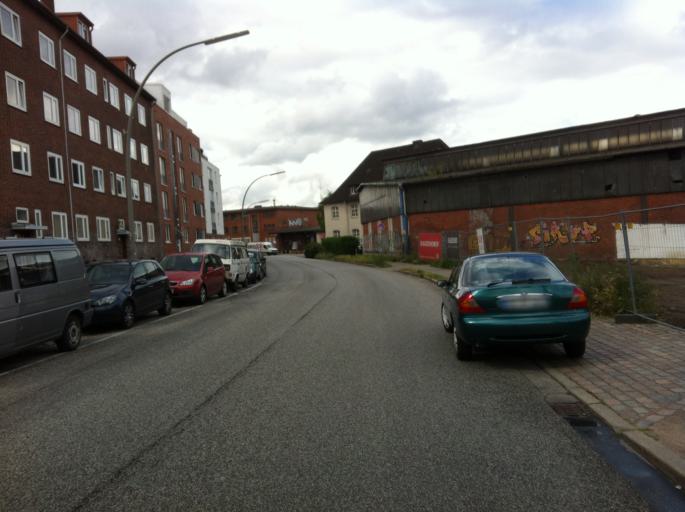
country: DE
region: Hamburg
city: Altona
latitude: 53.5580
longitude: 9.9381
